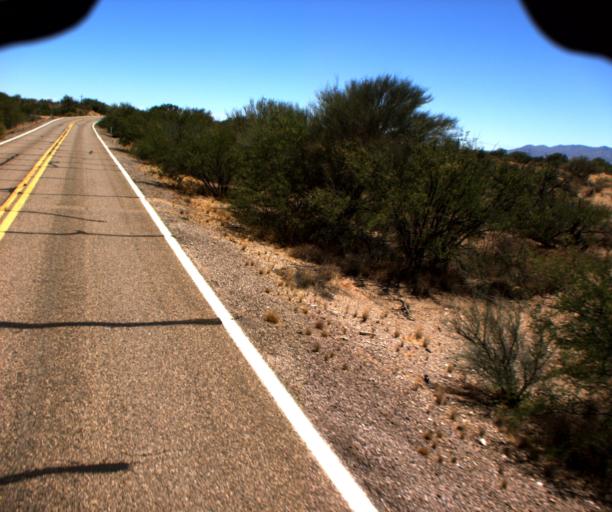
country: US
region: Arizona
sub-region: Pima County
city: Three Points
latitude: 31.9401
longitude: -111.3908
